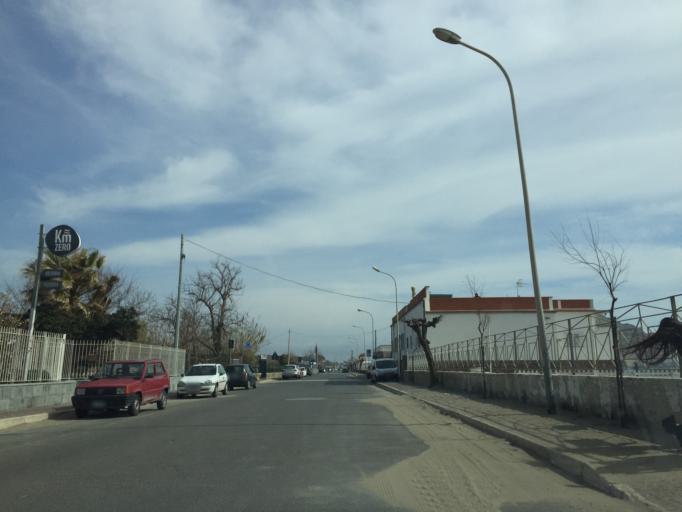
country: IT
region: Campania
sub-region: Provincia di Napoli
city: Bacoli
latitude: 40.7890
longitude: 14.0691
